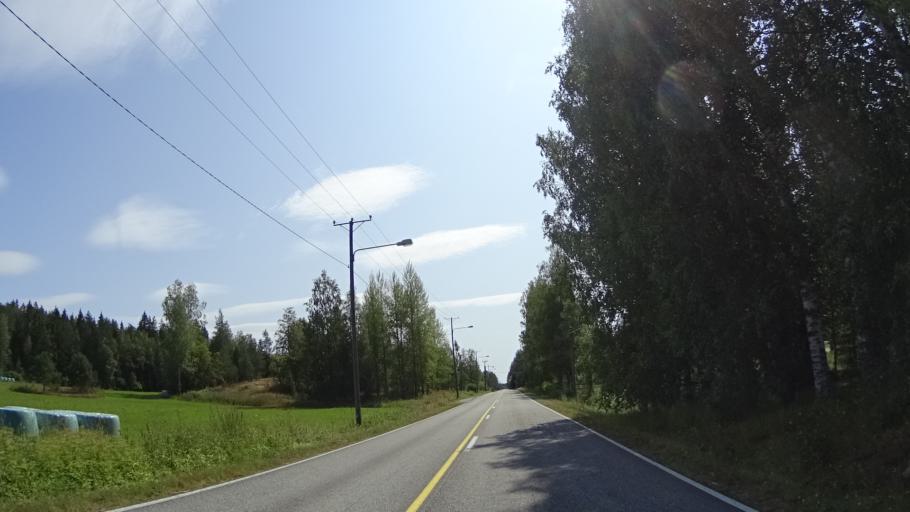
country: FI
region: Pirkanmaa
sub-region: Ylae-Pirkanmaa
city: Maenttae
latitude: 61.9078
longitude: 24.7858
